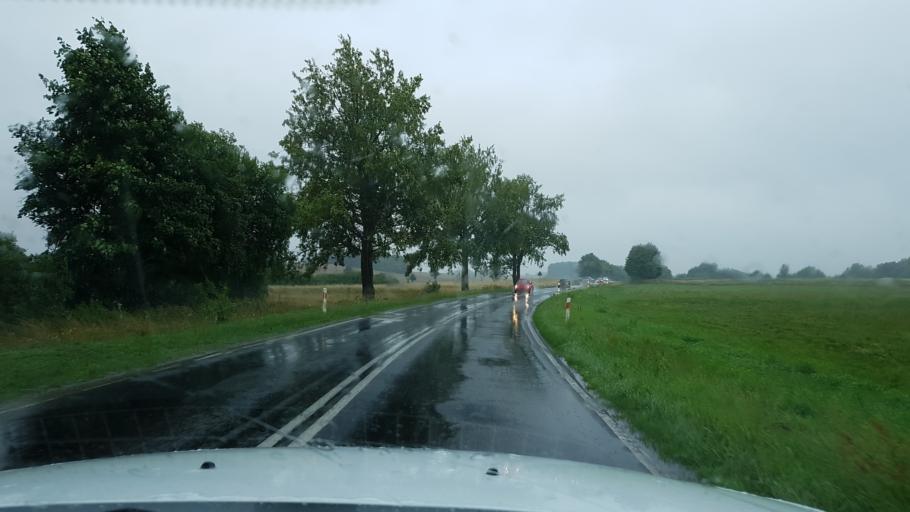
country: PL
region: West Pomeranian Voivodeship
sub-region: Powiat kolobrzeski
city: Grzybowo
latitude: 54.1018
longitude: 15.5132
